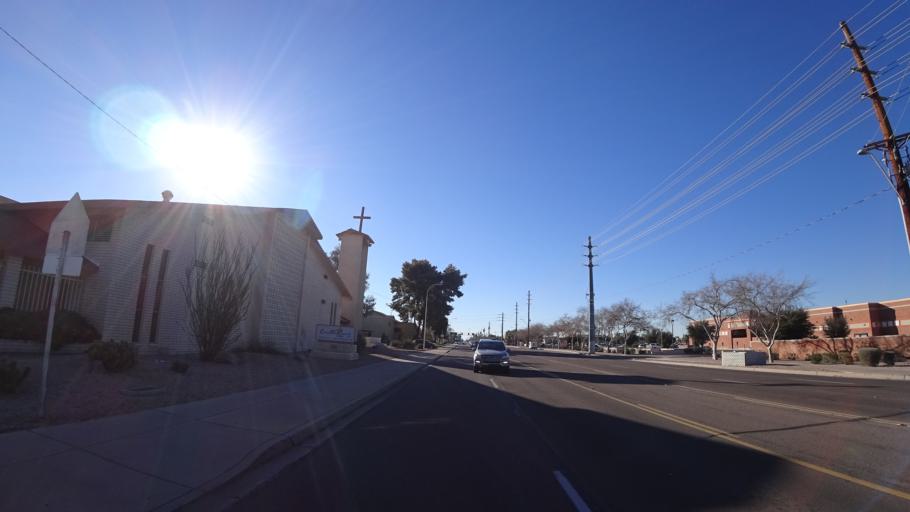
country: US
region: Arizona
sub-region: Maricopa County
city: Tempe
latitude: 33.3929
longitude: -111.9239
